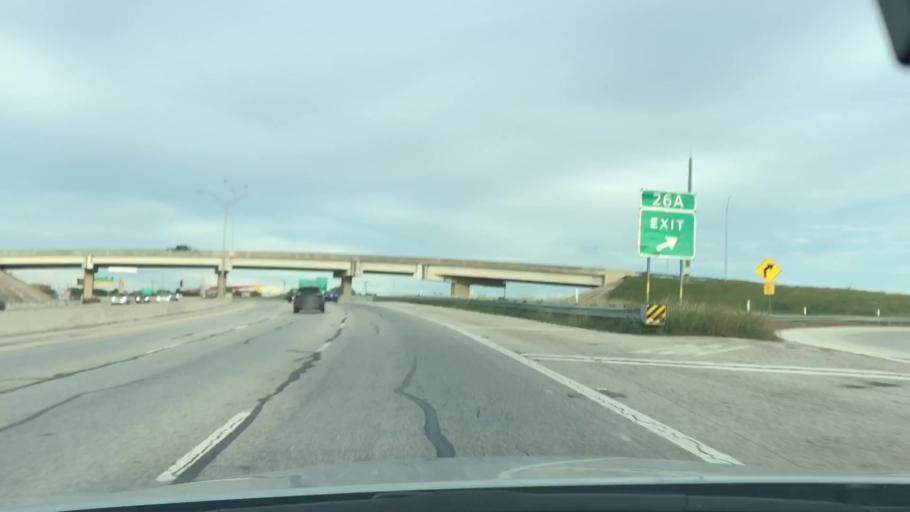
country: US
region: Texas
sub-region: Bexar County
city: Windcrest
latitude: 29.5159
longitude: -98.4043
